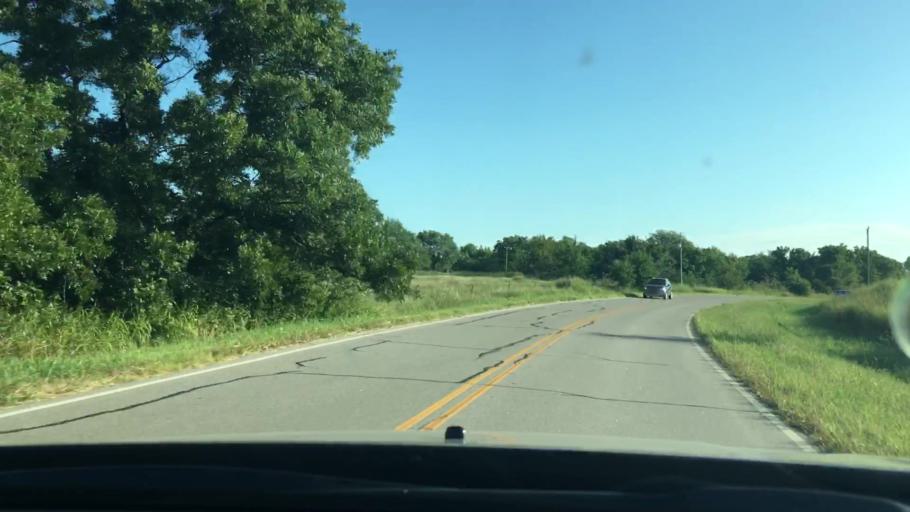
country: US
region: Oklahoma
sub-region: Pontotoc County
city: Ada
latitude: 34.6978
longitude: -96.4409
